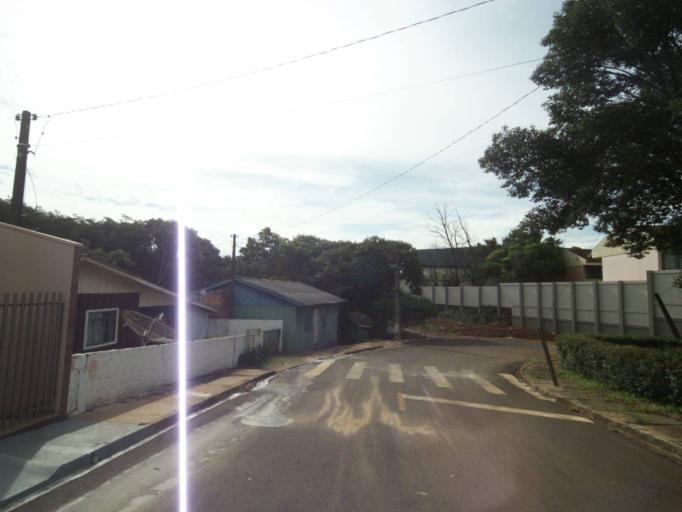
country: BR
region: Parana
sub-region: Guaraniacu
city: Guaraniacu
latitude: -25.1042
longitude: -52.8674
